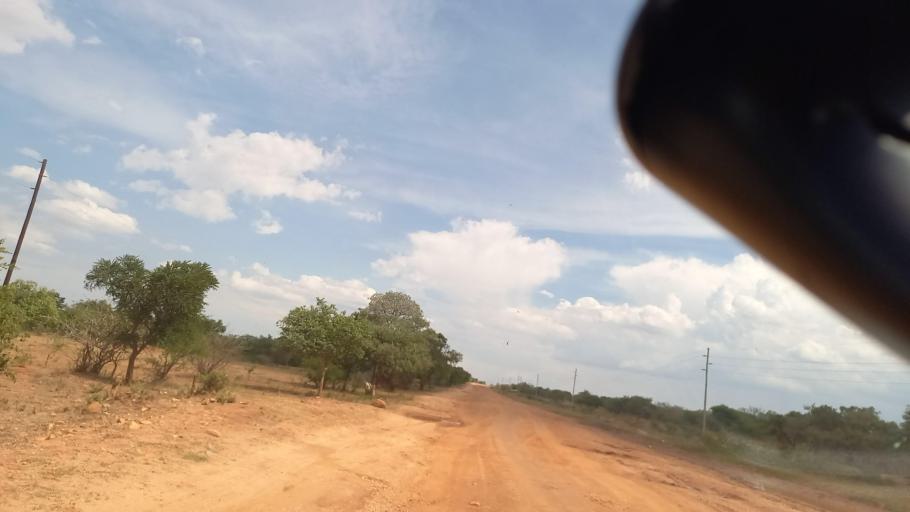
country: ZM
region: Lusaka
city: Kafue
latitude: -16.1395
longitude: 28.0525
